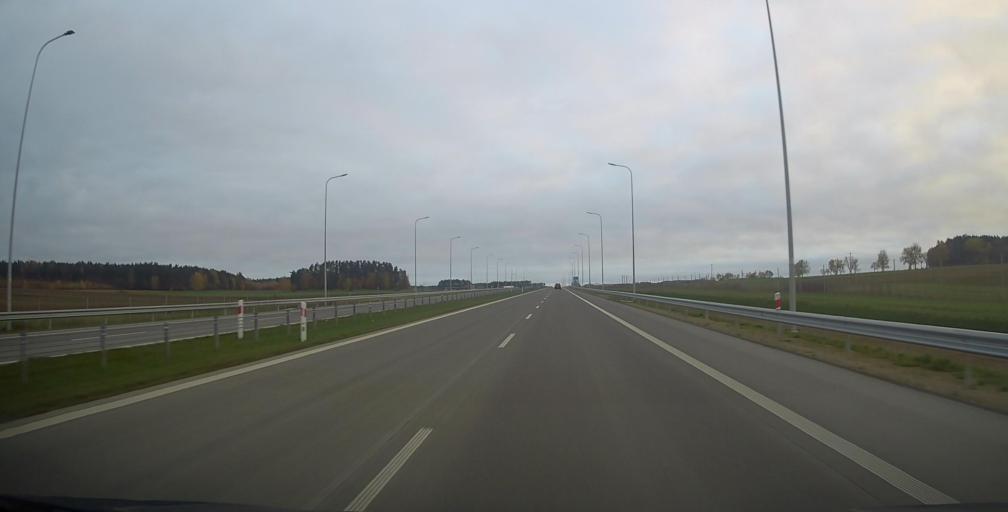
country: PL
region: Podlasie
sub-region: Powiat lomzynski
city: Piatnica
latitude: 53.2649
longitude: 22.1208
